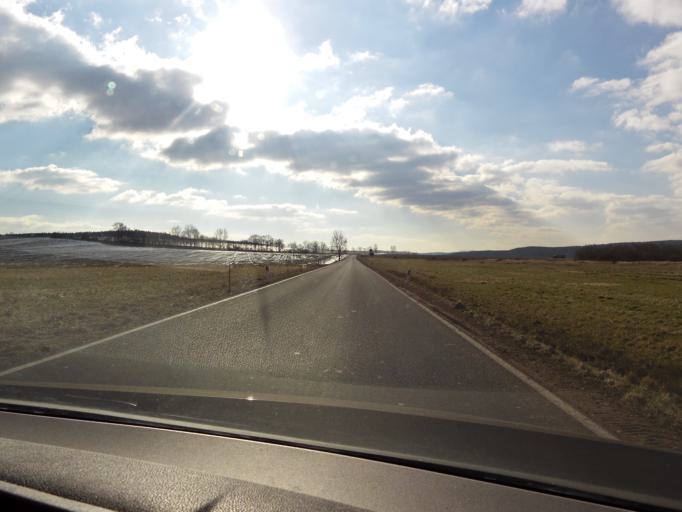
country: DE
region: Thuringia
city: Bad Salzungen
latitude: 50.8569
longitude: 10.2380
